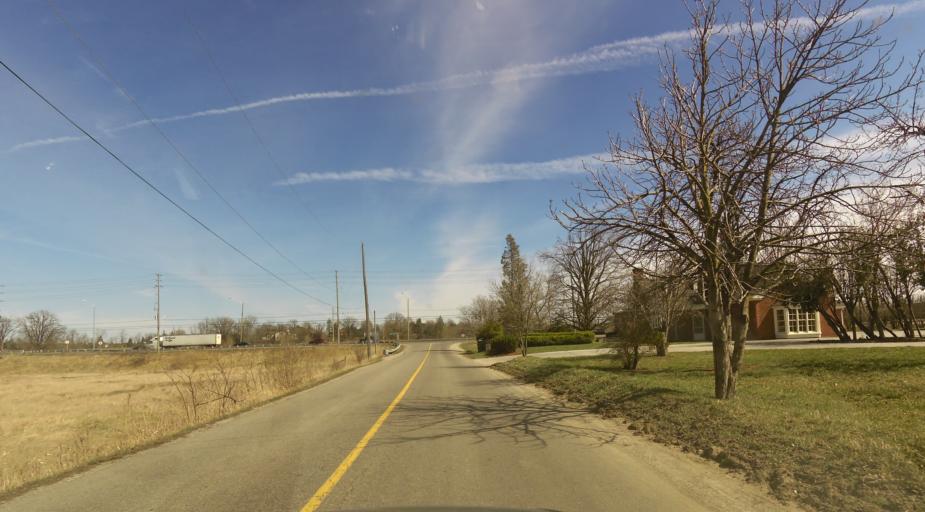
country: CA
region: Ontario
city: Brampton
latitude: 43.6377
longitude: -79.7666
